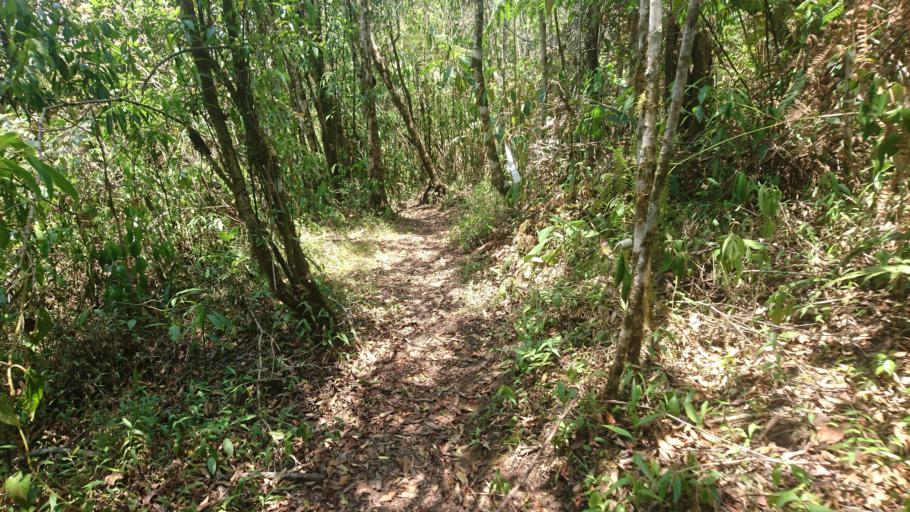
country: GT
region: Huehuetenango
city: Union
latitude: 16.1091
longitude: -91.6723
